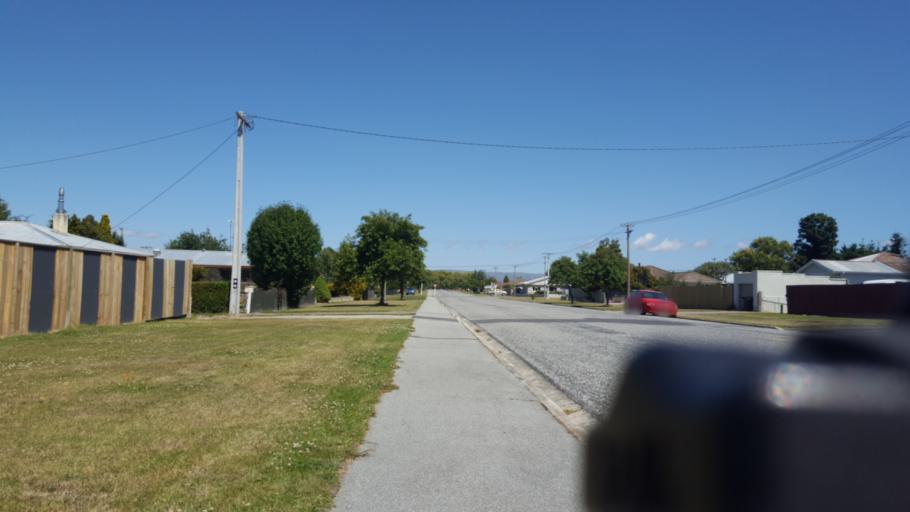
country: NZ
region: Otago
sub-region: Dunedin City
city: Dunedin
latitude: -45.1269
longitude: 170.1023
